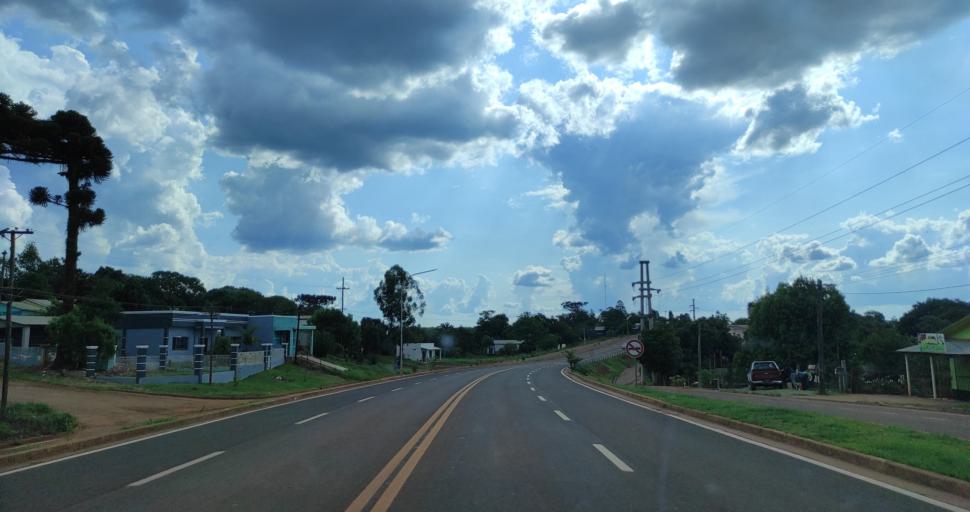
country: AR
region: Misiones
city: Bernardo de Irigoyen
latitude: -26.2952
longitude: -53.7480
